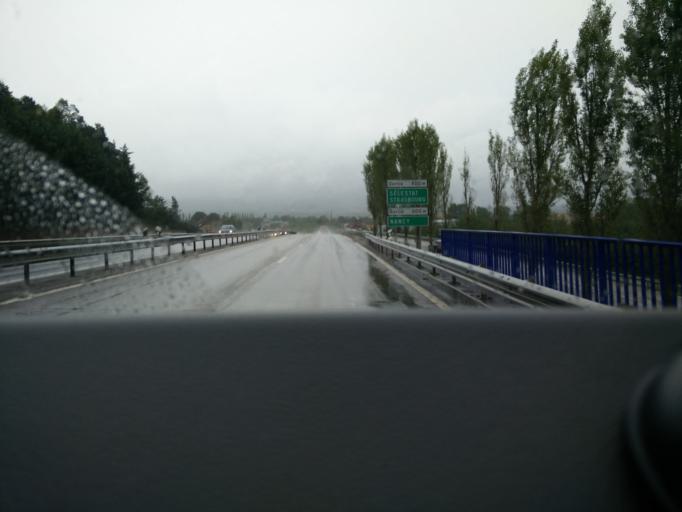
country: FR
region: Lorraine
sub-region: Departement des Vosges
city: Saulcy-sur-Meurthe
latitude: 48.2563
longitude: 6.9601
